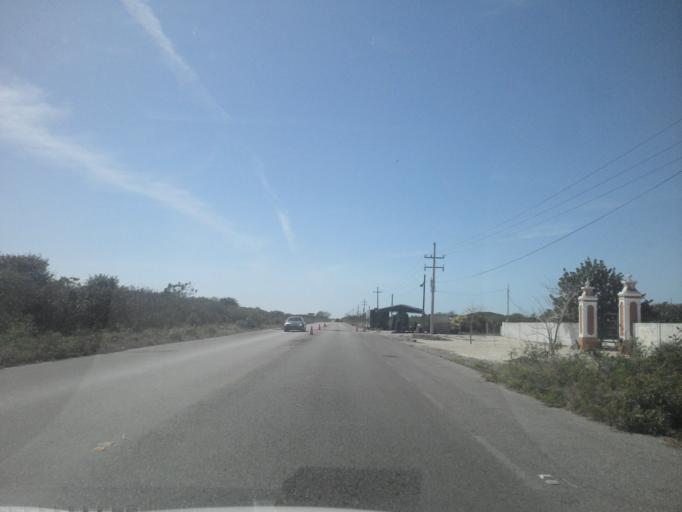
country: MX
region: Yucatan
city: Telchac Puerto
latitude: 21.3325
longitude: -89.3535
